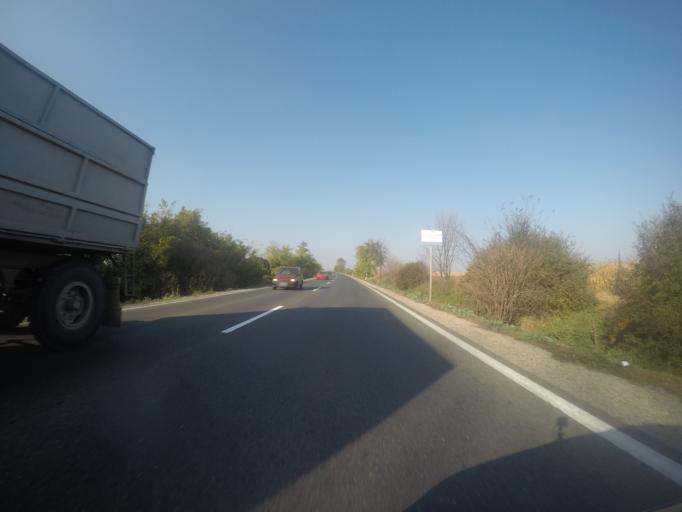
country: HU
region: Fejer
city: Racalmas
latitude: 47.0052
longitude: 18.9307
